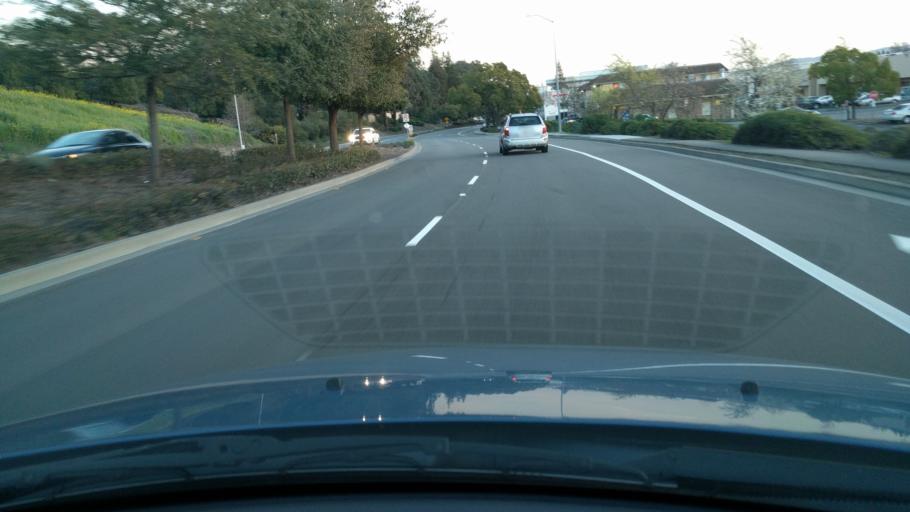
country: US
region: California
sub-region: Contra Costa County
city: San Ramon
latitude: 37.7796
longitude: -121.9636
